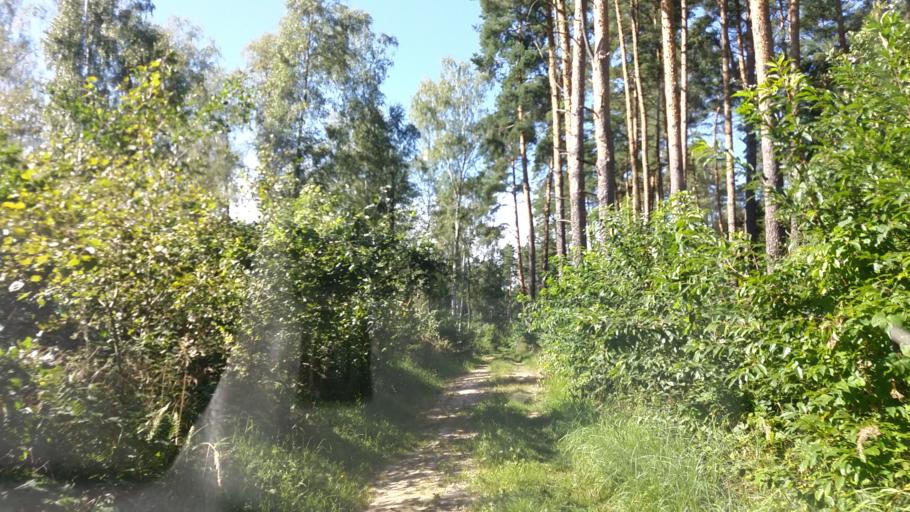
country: PL
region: West Pomeranian Voivodeship
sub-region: Powiat choszczenski
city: Krzecin
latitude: 53.0845
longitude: 15.4611
